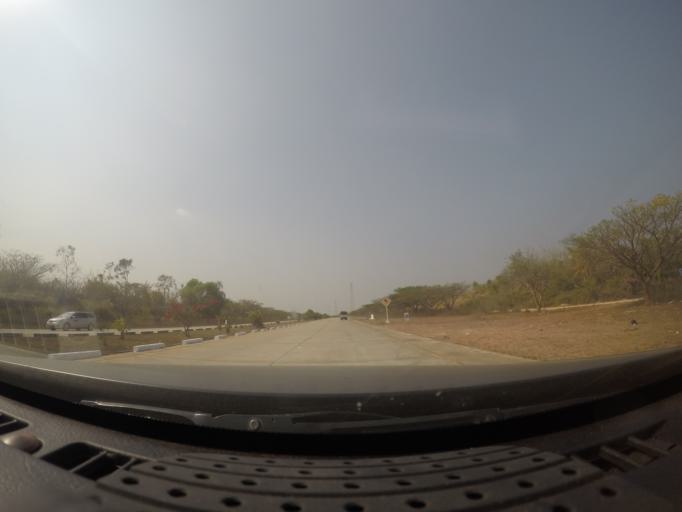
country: MM
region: Mandalay
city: Nay Pyi Taw
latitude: 20.0066
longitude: 95.9600
